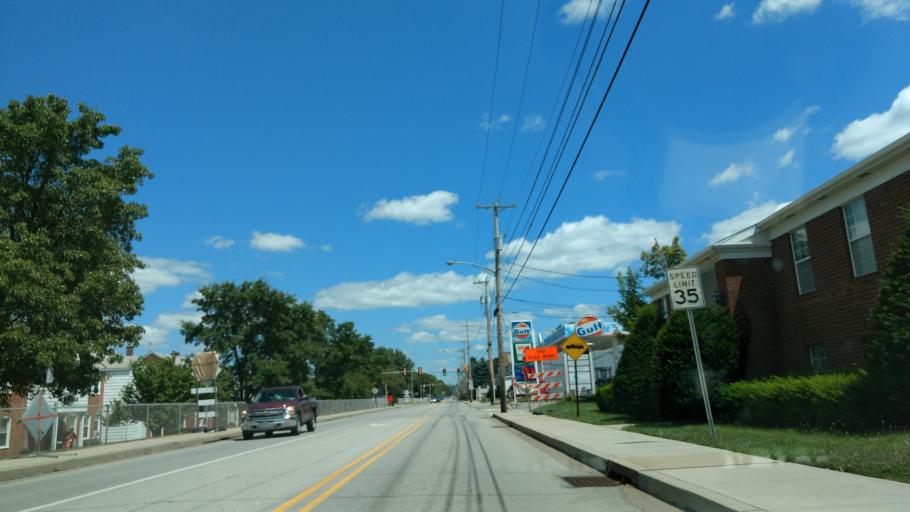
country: US
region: Pennsylvania
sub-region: Beaver County
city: Beaver
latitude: 40.6844
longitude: -80.3295
